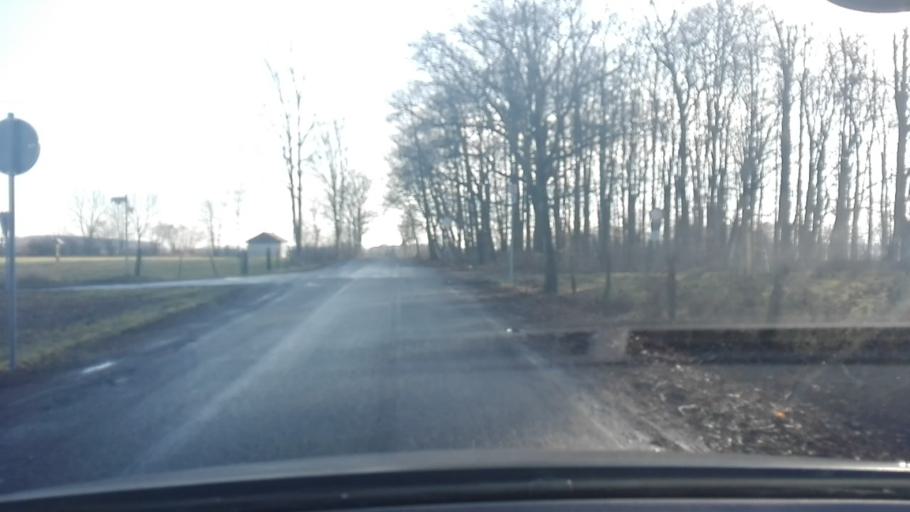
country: DE
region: North Rhine-Westphalia
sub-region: Regierungsbezirk Arnsberg
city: Frondenberg
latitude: 51.4988
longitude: 7.7648
